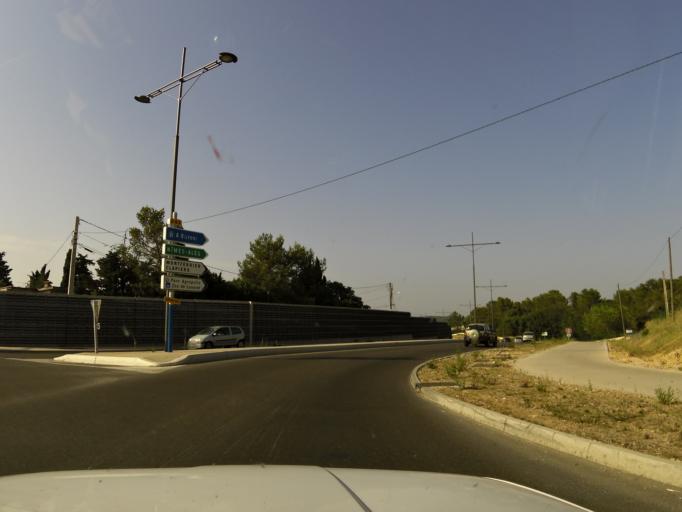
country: FR
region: Languedoc-Roussillon
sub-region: Departement de l'Herault
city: Montferrier-sur-Lez
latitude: 43.6450
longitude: 3.8529
